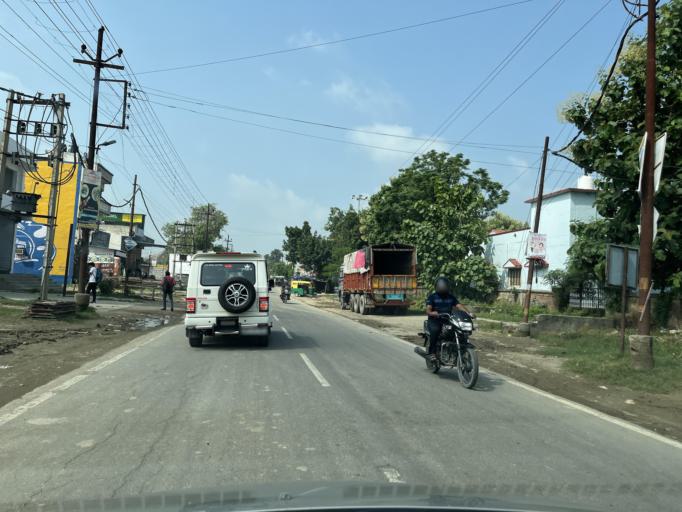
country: IN
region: Uttarakhand
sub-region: Udham Singh Nagar
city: Bazpur
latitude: 29.1637
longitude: 79.1573
